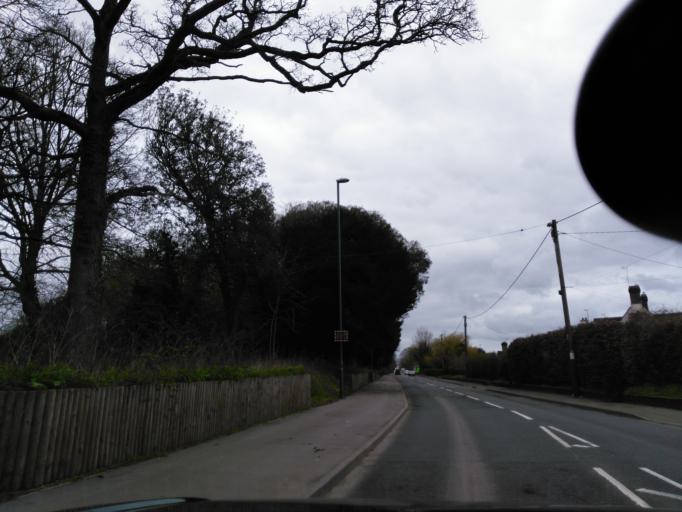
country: GB
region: England
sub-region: Gloucestershire
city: Cirencester
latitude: 51.7188
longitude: -1.9570
